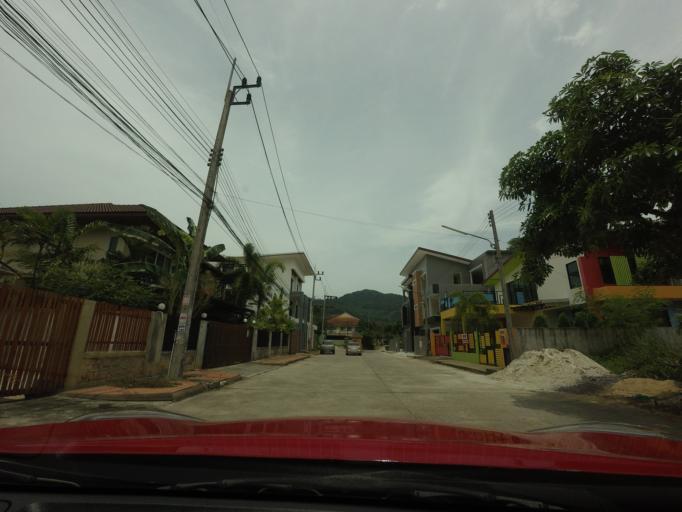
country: TH
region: Songkhla
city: Na Mom
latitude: 7.0032
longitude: 100.5310
